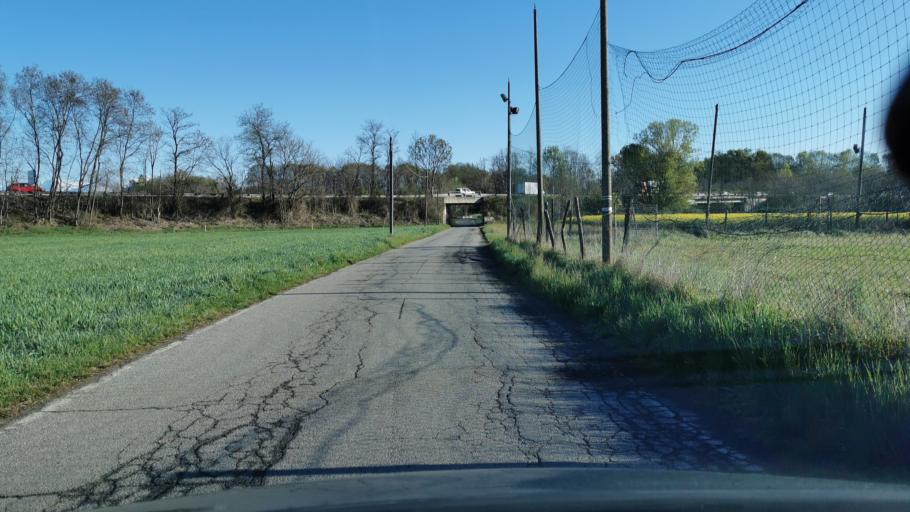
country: IT
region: Piedmont
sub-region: Provincia di Torino
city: Leini
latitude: 45.2070
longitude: 7.7142
